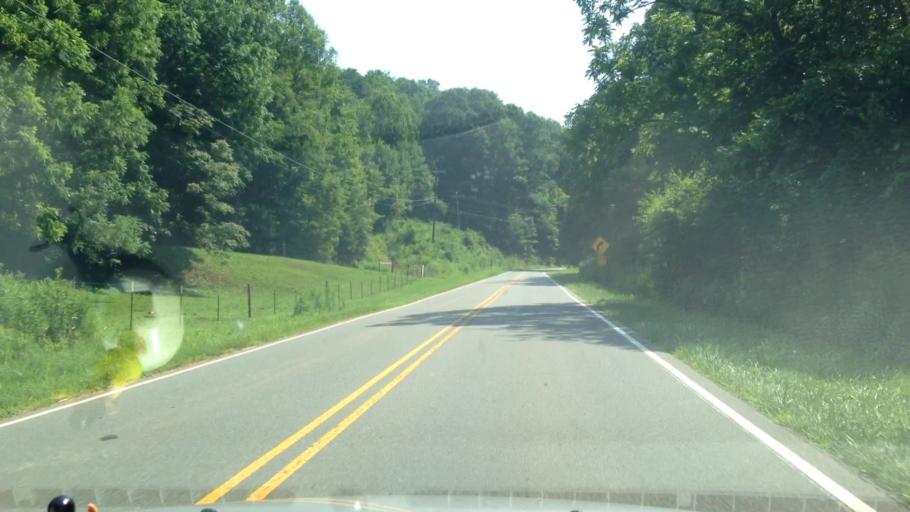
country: US
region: North Carolina
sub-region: Surry County
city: Flat Rock
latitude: 36.5357
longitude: -80.5200
